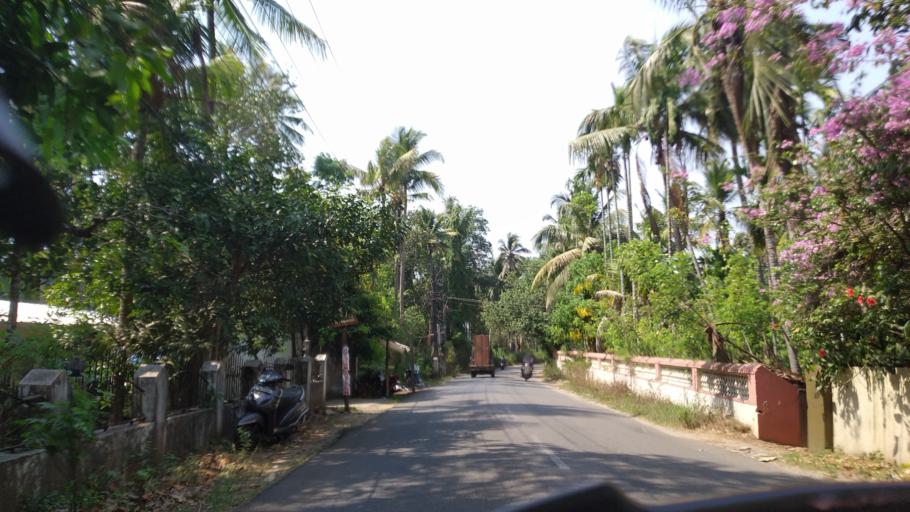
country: IN
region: Kerala
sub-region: Thrissur District
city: Kodungallur
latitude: 10.2455
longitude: 76.1495
